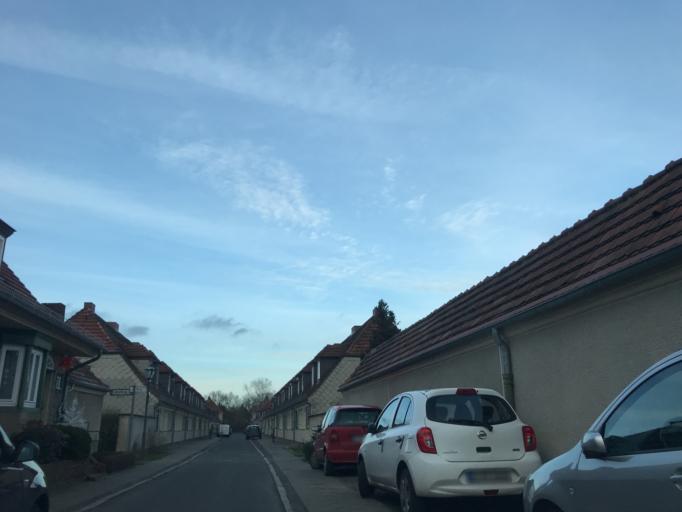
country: DE
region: Berlin
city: Staaken
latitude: 52.5412
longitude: 13.1489
